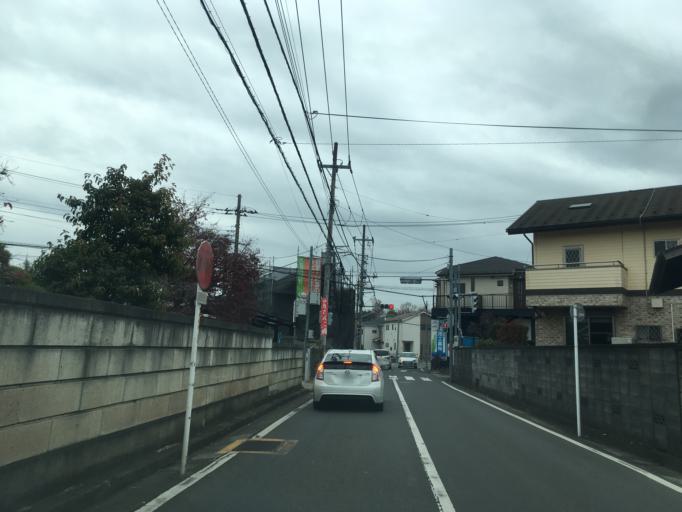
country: JP
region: Tokyo
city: Higashimurayama-shi
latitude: 35.7674
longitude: 139.4747
